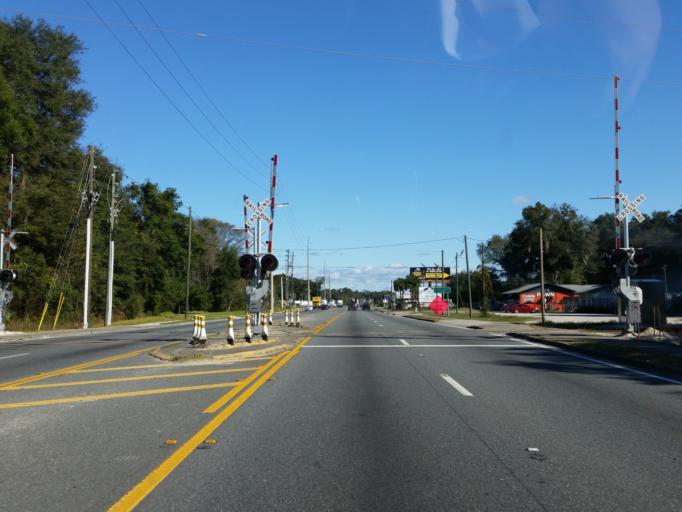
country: US
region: Florida
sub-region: Marion County
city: Ocala
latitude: 29.2669
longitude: -82.1835
